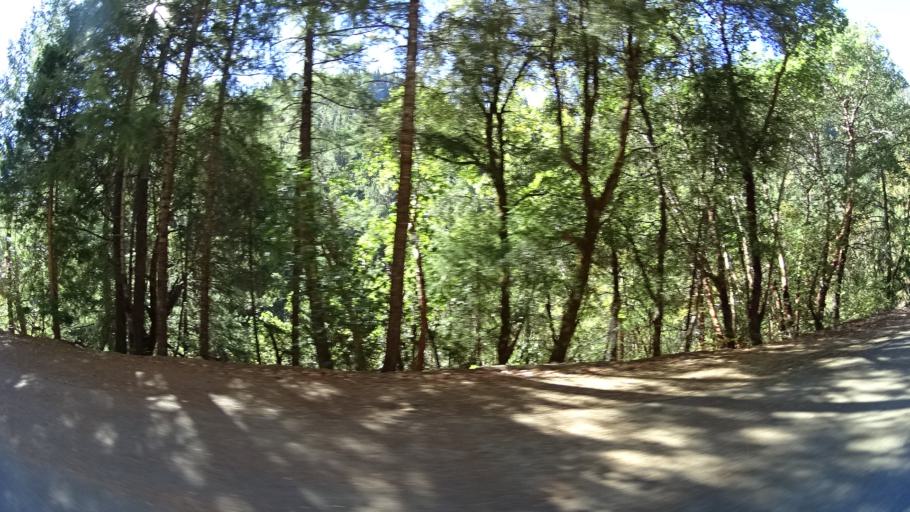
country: US
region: California
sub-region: Humboldt County
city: Willow Creek
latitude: 41.1459
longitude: -123.1960
